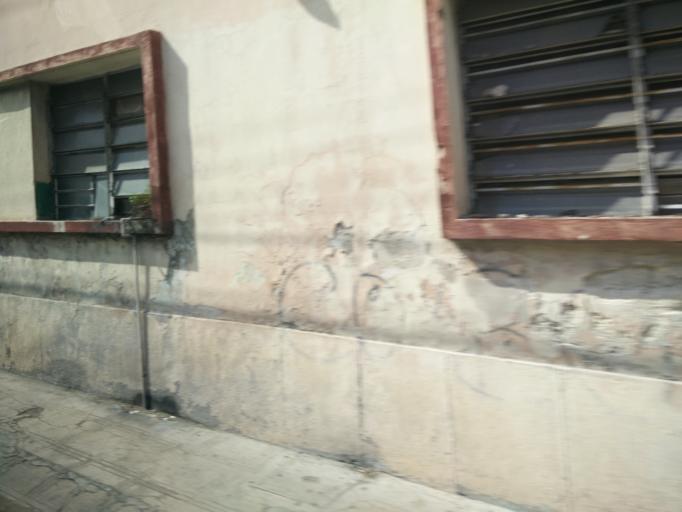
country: MX
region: Yucatan
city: Merida
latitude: 20.9661
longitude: -89.6144
